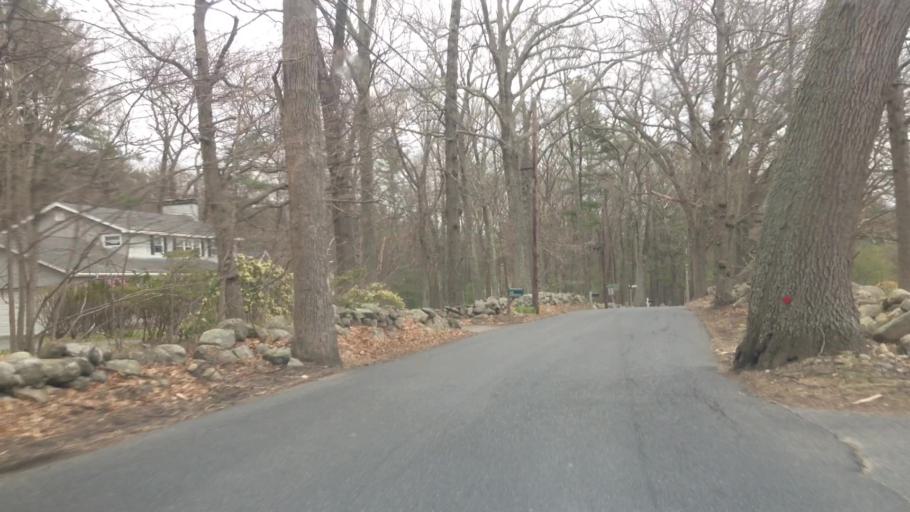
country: US
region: Massachusetts
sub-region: Middlesex County
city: West Concord
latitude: 42.4916
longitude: -71.3949
